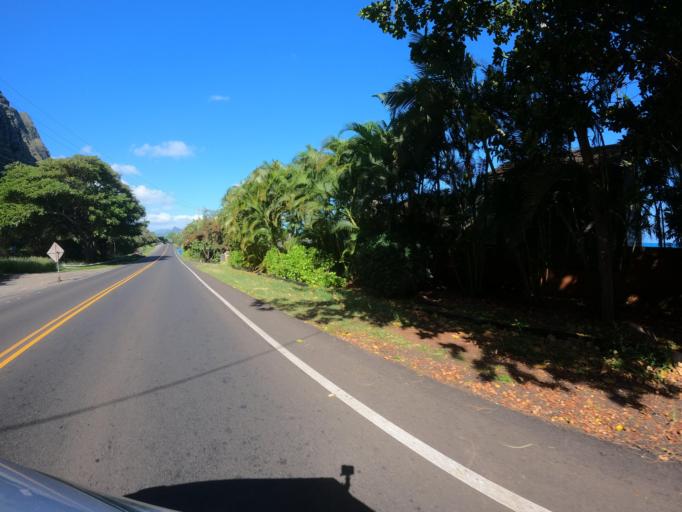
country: US
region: Hawaii
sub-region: Honolulu County
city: Waimanalo Beach
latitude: 21.3229
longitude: -157.6764
